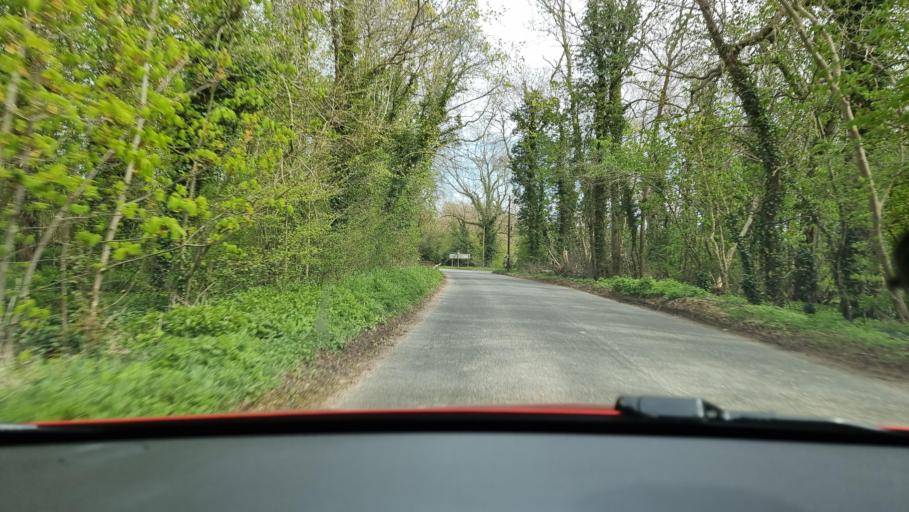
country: GB
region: England
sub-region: Oxfordshire
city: Oxford
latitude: 51.8075
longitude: -1.2195
